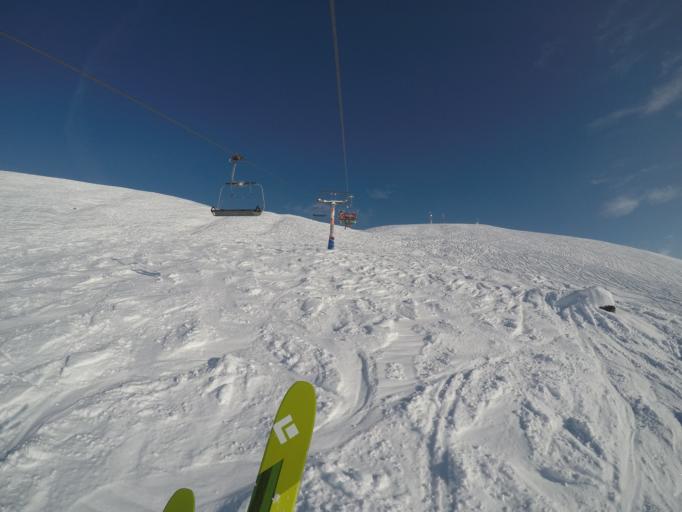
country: GE
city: Gudauri
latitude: 42.4852
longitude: 44.4963
